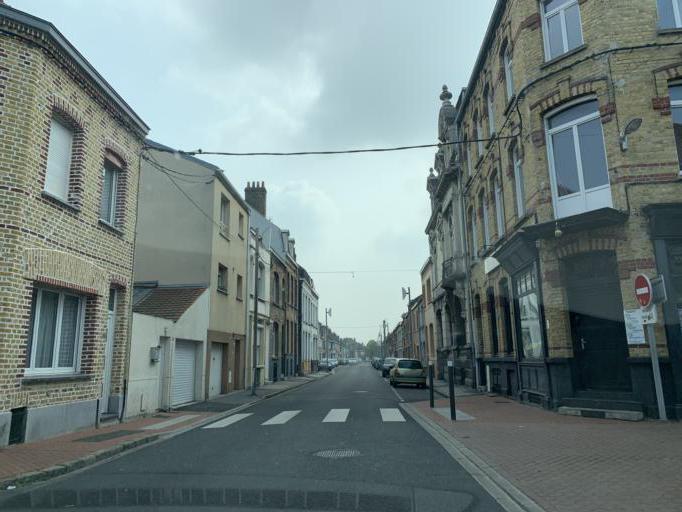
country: FR
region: Nord-Pas-de-Calais
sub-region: Departement du Nord
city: Coudekerque-Branche
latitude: 51.0425
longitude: 2.3981
